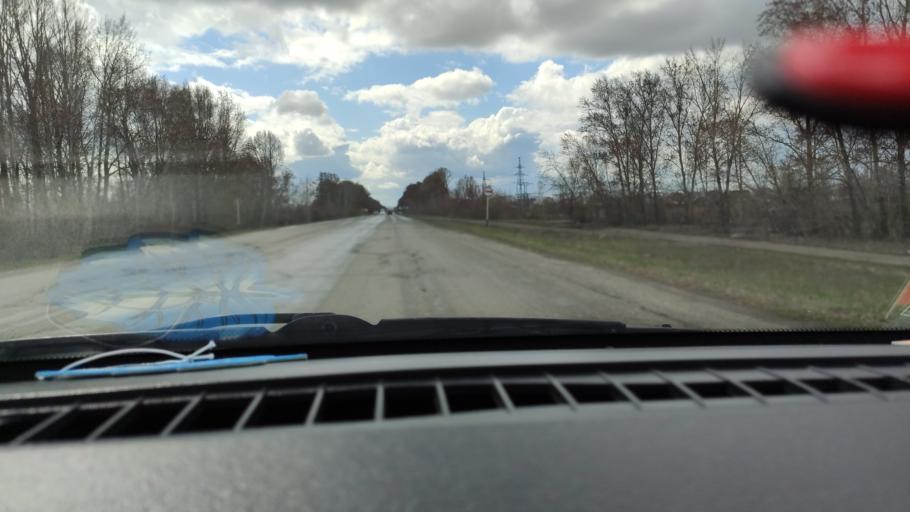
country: RU
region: Samara
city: Tol'yatti
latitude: 53.6299
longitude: 49.4171
